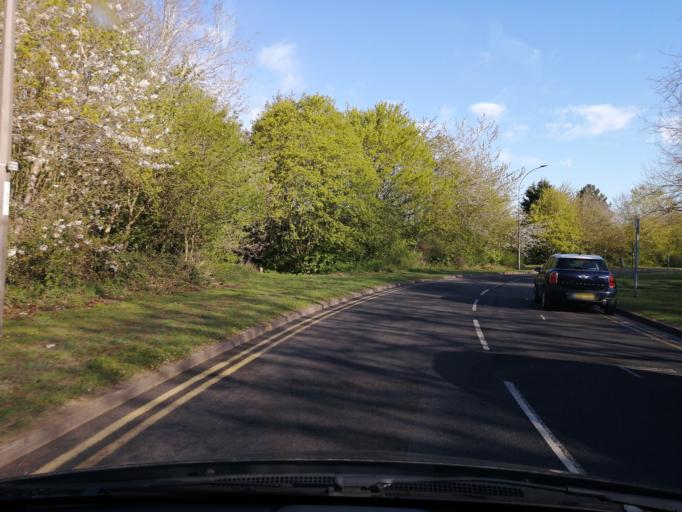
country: GB
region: England
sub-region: Peterborough
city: Castor
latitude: 52.5561
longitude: -0.3180
